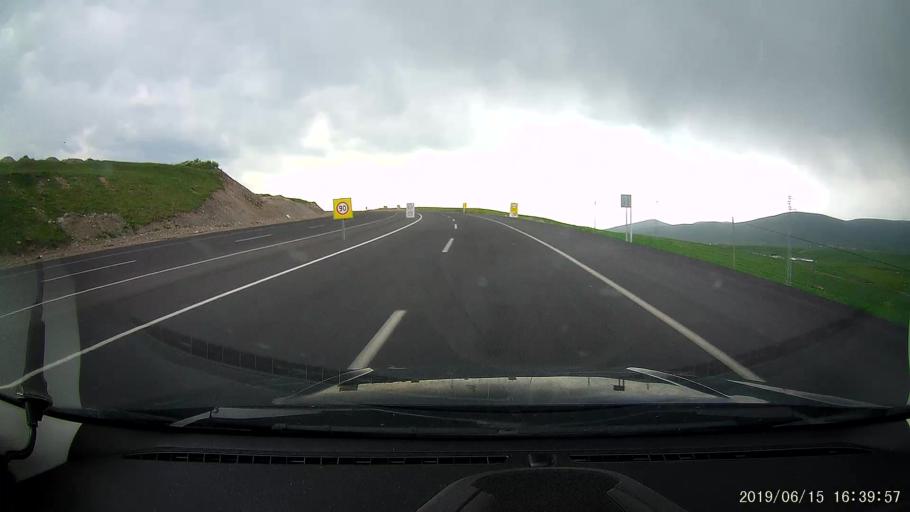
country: TR
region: Ardahan
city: Haskoy
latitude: 40.9759
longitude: 42.8933
